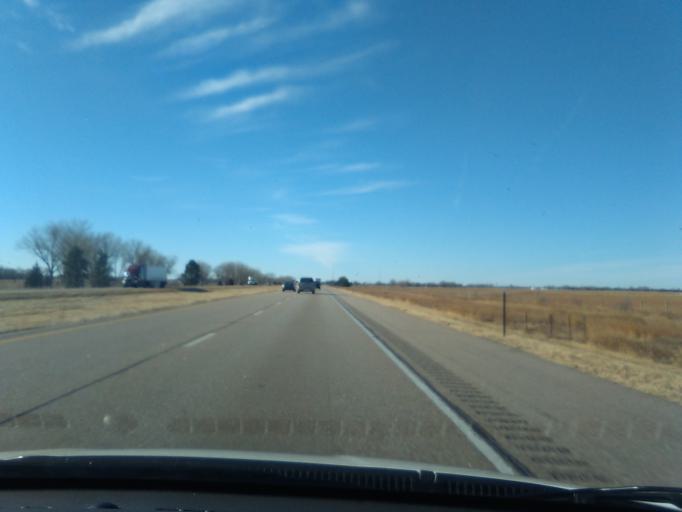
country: US
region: Nebraska
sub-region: Hall County
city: Wood River
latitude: 40.7682
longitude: -98.5701
